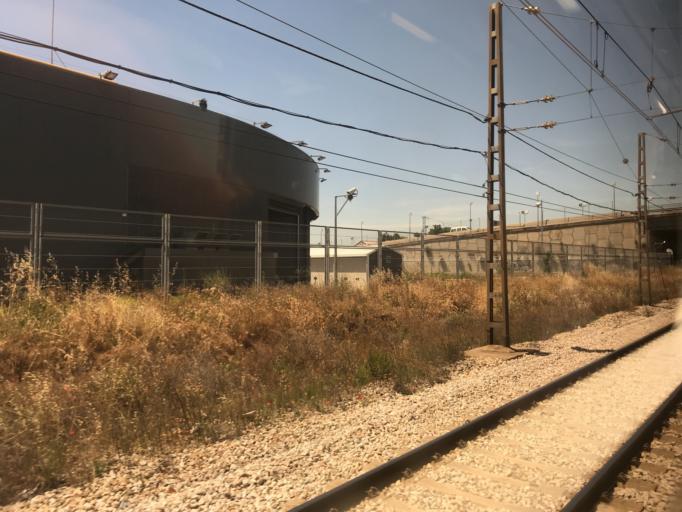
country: ES
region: Madrid
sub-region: Provincia de Madrid
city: Getafe
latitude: 40.3040
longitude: -3.7076
